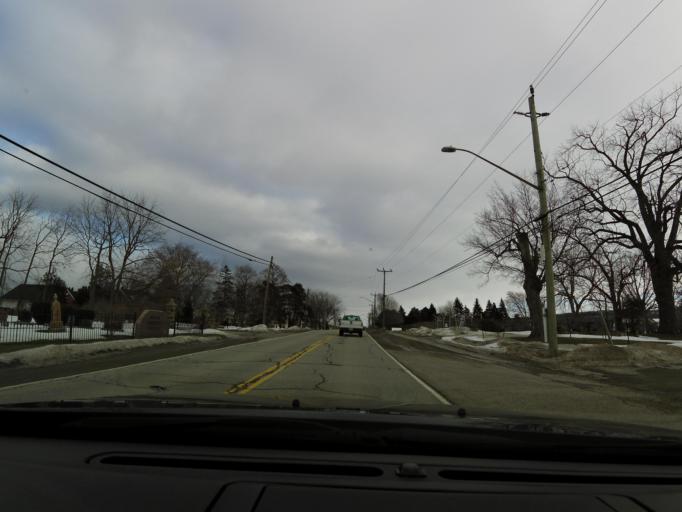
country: CA
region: Ontario
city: Hamilton
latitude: 43.2069
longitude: -79.6343
